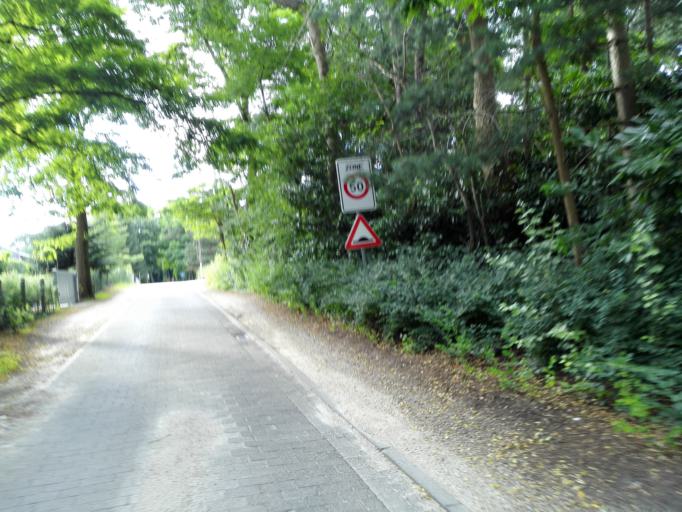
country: BE
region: Flanders
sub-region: Provincie Vlaams-Brabant
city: Keerbergen
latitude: 51.0091
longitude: 4.6117
